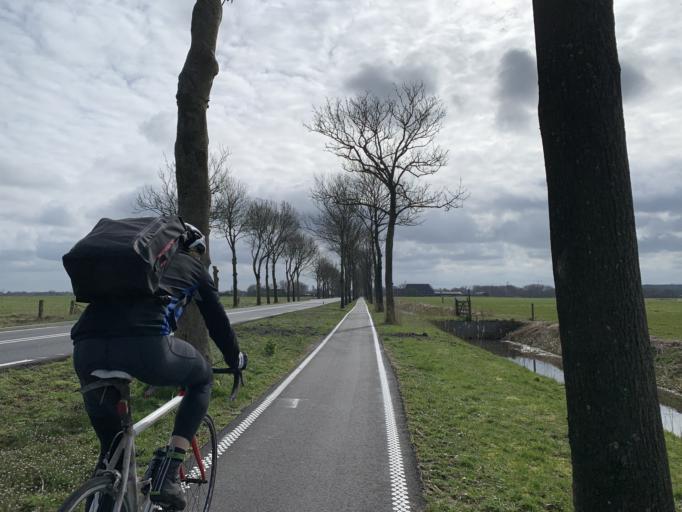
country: NL
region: Groningen
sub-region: Gemeente Groningen
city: Korrewegwijk
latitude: 53.2575
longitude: 6.5402
